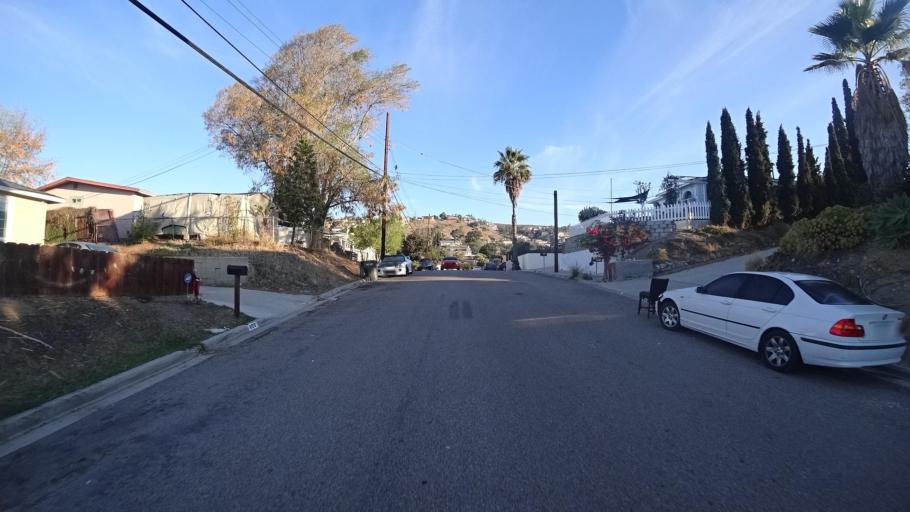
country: US
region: California
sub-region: San Diego County
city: La Presa
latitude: 32.7136
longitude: -116.9931
